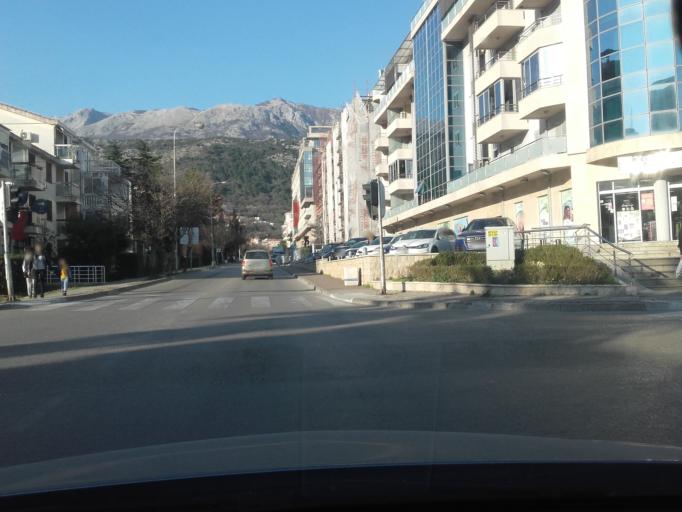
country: ME
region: Budva
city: Budva
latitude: 42.2902
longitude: 18.8369
